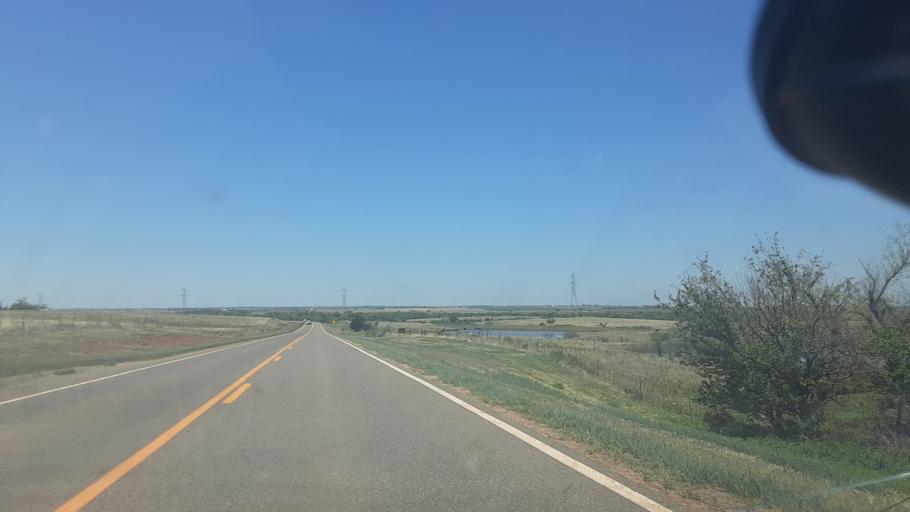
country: US
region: Oklahoma
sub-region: Noble County
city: Perry
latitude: 36.1157
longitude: -97.3640
